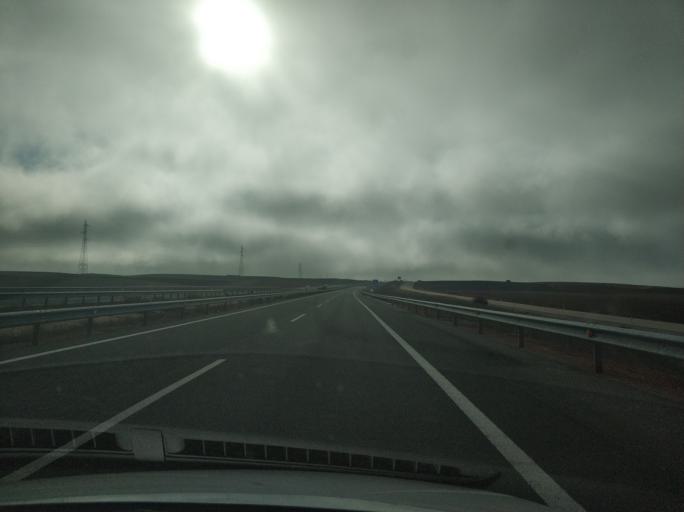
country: ES
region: Castille and Leon
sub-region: Provincia de Soria
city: Alcubilla de las Penas
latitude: 41.2800
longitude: -2.4757
